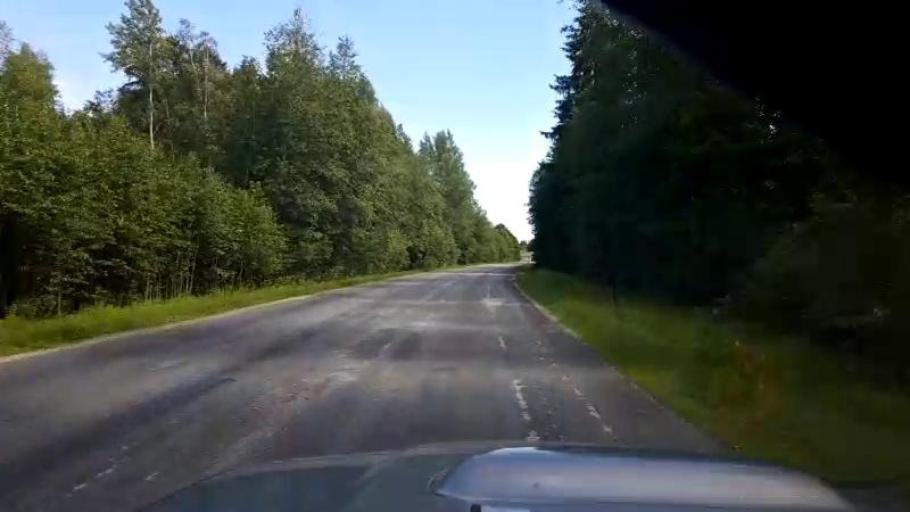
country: EE
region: Laeaene-Virumaa
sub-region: Rakke vald
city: Rakke
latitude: 58.9129
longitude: 26.2709
